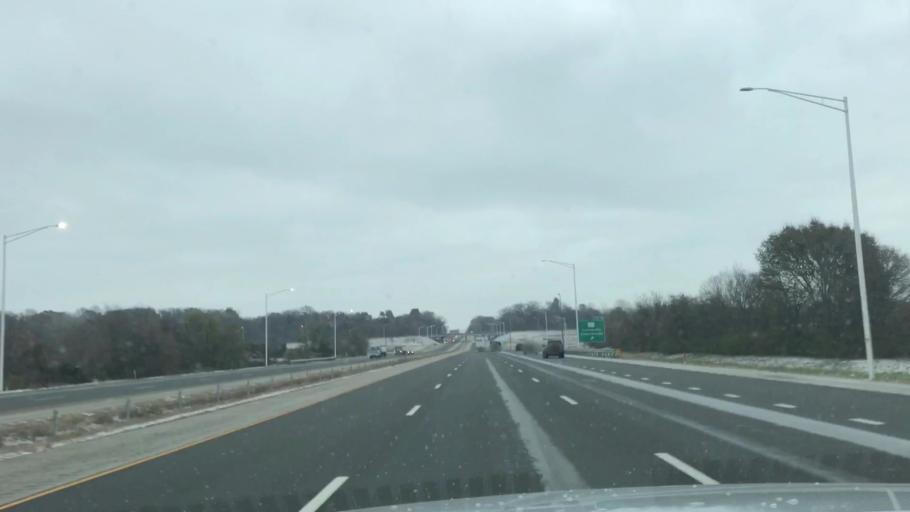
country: US
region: Illinois
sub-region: Madison County
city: Glen Carbon
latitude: 38.7566
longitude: -90.0163
